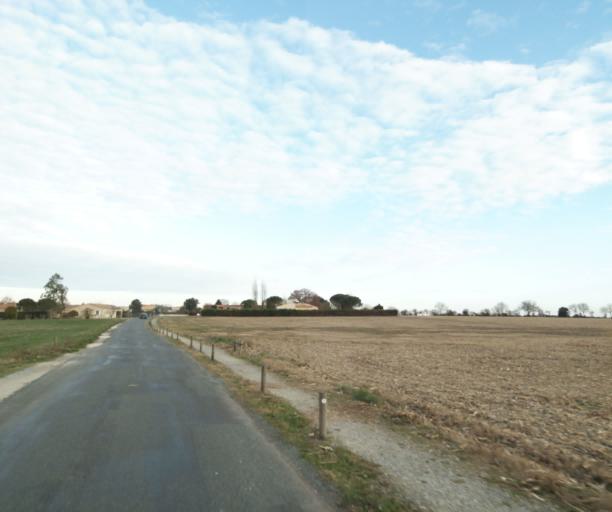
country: FR
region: Poitou-Charentes
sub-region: Departement de la Charente-Maritime
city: Les Gonds
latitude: 45.7105
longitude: -0.6148
